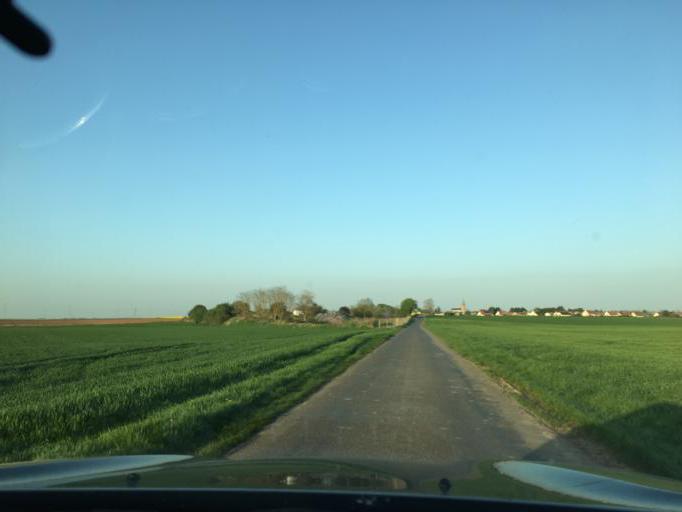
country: FR
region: Centre
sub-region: Departement du Loiret
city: Beaugency
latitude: 47.7997
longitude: 1.5852
